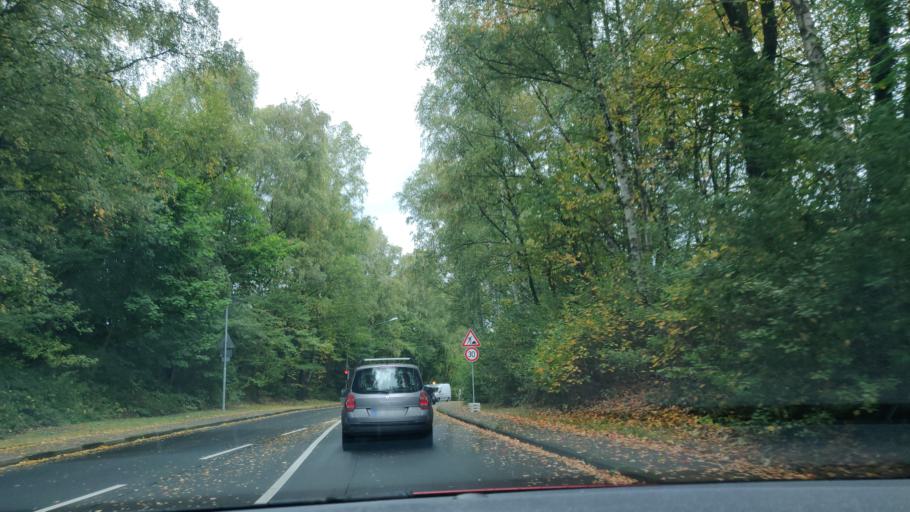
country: DE
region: North Rhine-Westphalia
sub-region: Regierungsbezirk Dusseldorf
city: Heiligenhaus
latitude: 51.2951
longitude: 6.9270
